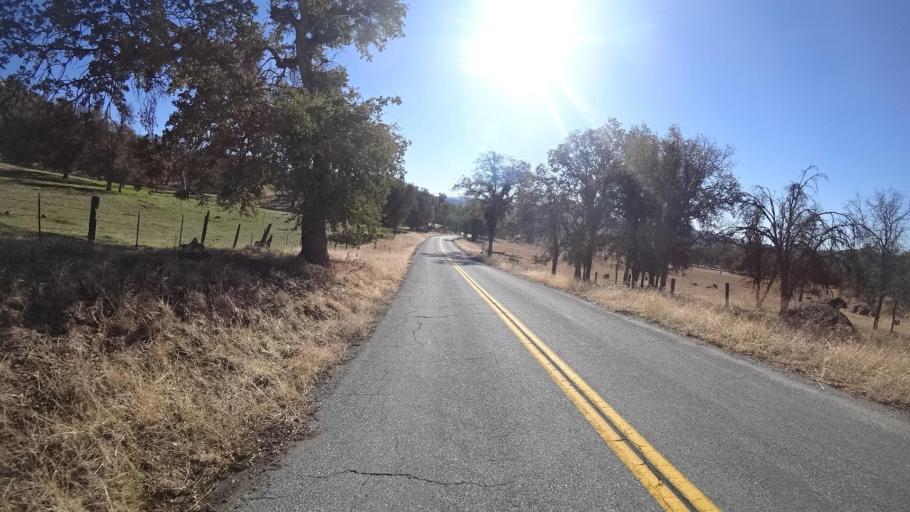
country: US
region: California
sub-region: Kern County
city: Alta Sierra
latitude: 35.7973
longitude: -118.7122
